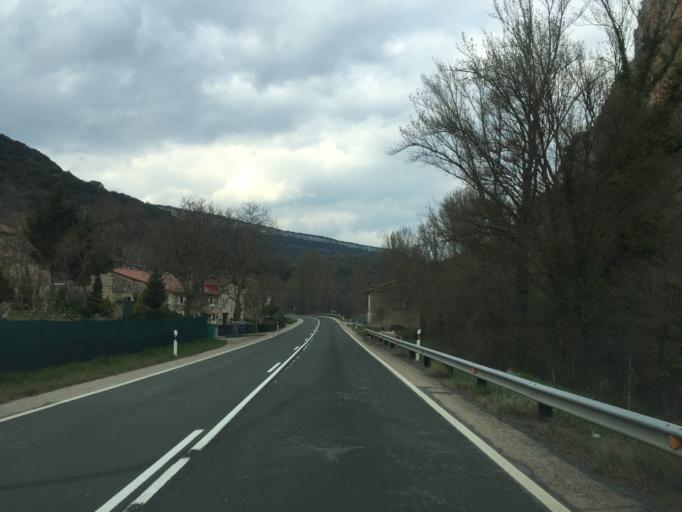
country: ES
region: Castille and Leon
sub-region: Provincia de Burgos
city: Tubilla del Agua
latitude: 42.7602
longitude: -3.7982
